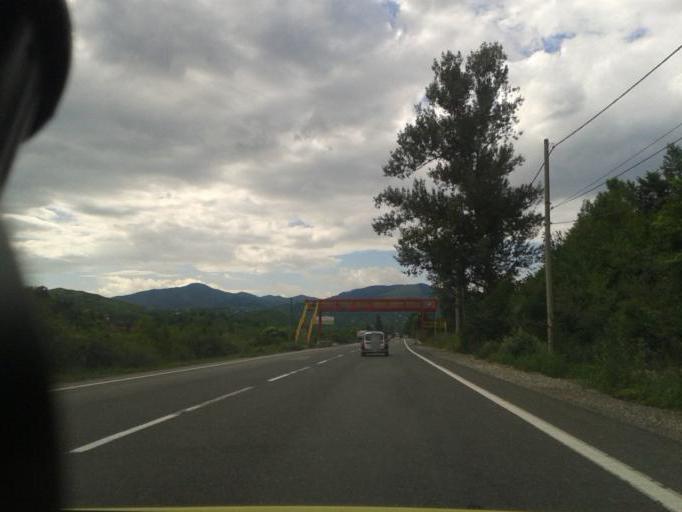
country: RO
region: Prahova
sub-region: Oras Breaza
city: Gura Beliei
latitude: 45.2132
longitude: 25.6531
